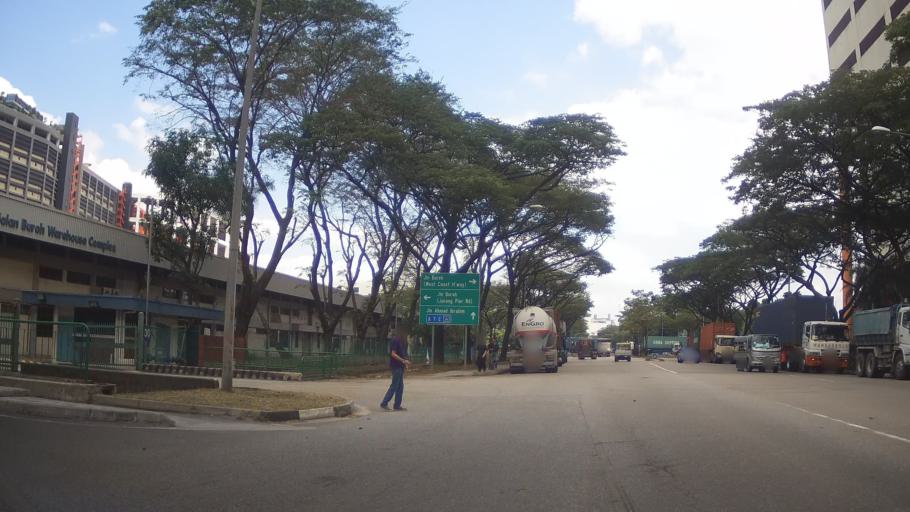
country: SG
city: Singapore
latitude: 1.3124
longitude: 103.7191
